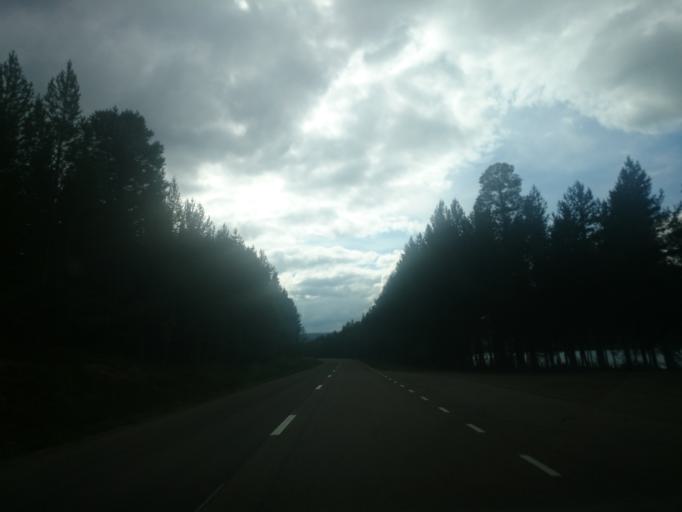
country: SE
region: Jaemtland
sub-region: Harjedalens Kommun
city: Sveg
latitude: 62.3394
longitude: 13.7741
